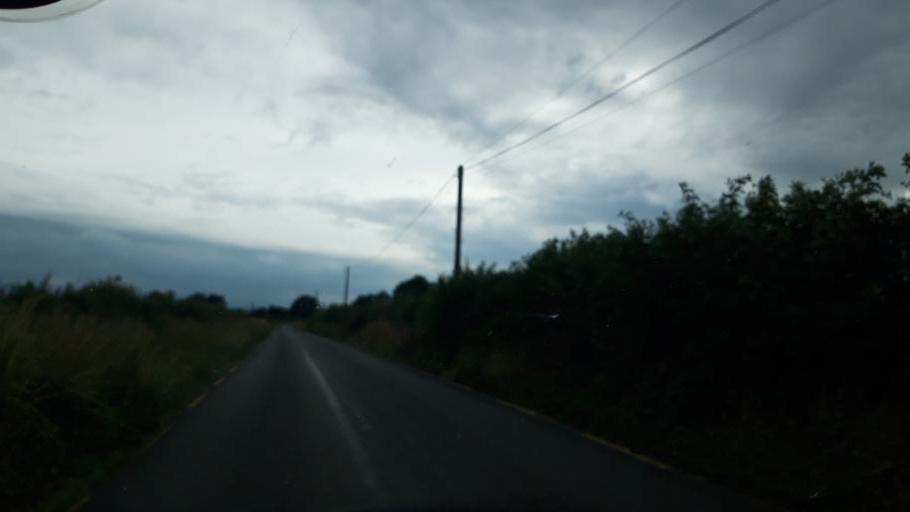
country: IE
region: Leinster
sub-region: Kilkenny
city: Ballyragget
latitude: 52.7782
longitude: -7.3446
